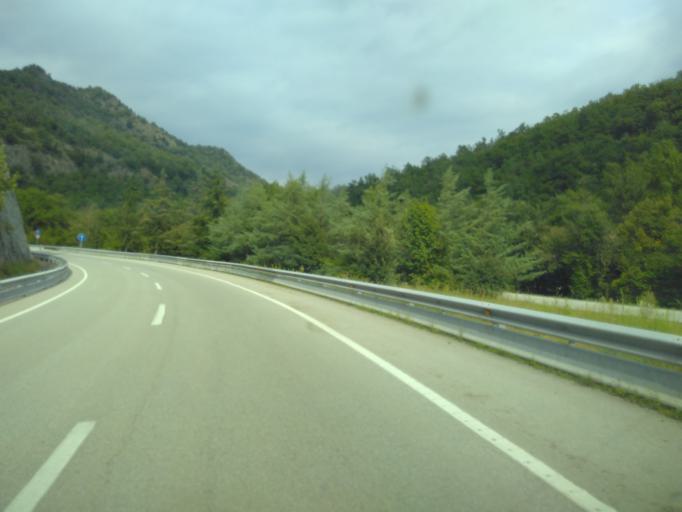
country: ES
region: Catalonia
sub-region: Provincia de Barcelona
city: Montesquiu
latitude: 42.1369
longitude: 2.2099
